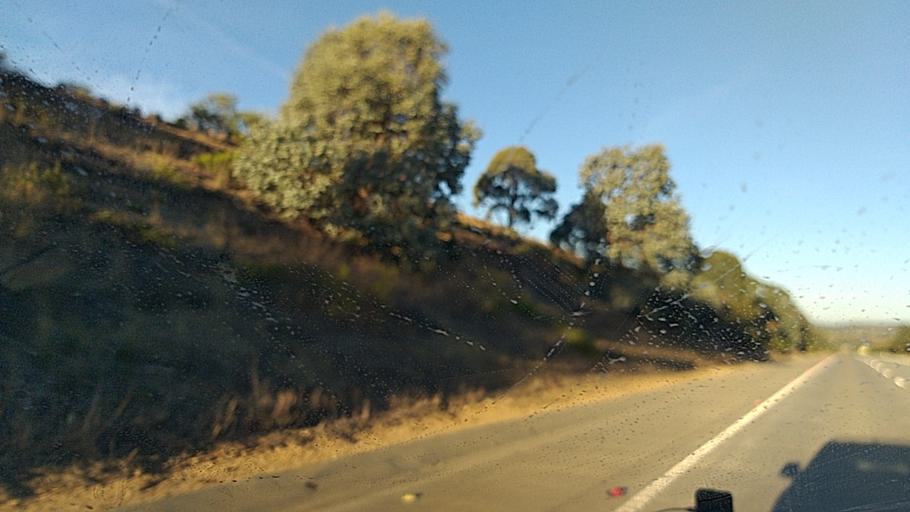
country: AU
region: New South Wales
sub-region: Yass Valley
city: Gundaroo
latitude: -35.1135
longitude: 149.3620
